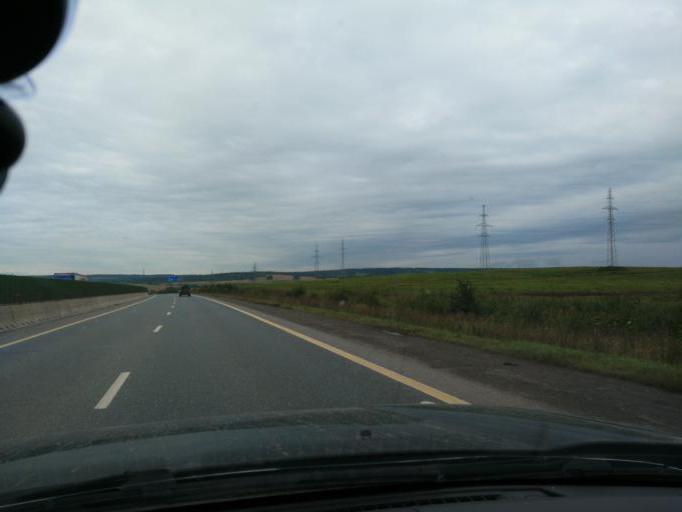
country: RU
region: Perm
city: Ferma
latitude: 57.9299
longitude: 56.3176
